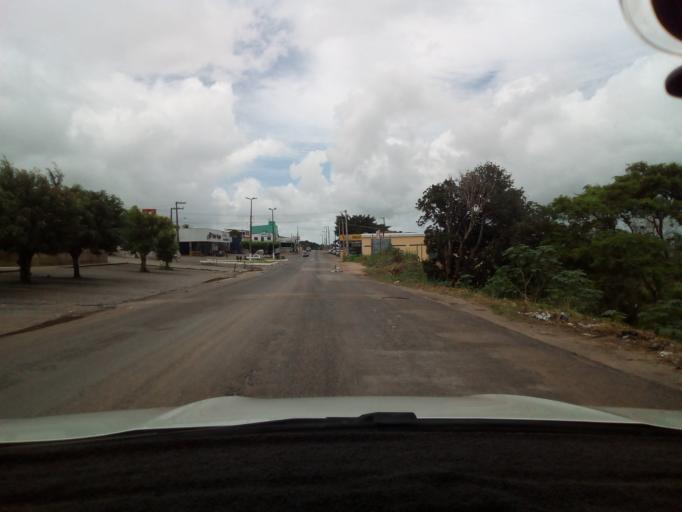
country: BR
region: Paraiba
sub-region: Pedras De Fogo
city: Pedras de Fogo
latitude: -7.4051
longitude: -35.1214
